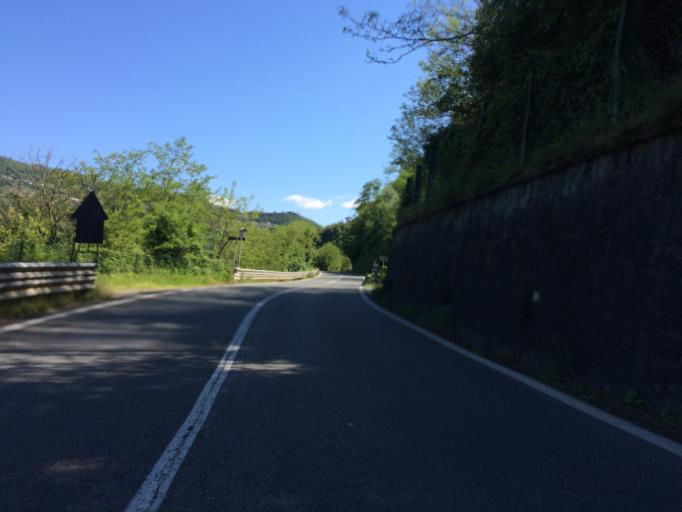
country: IT
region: Tuscany
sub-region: Provincia di Massa-Carrara
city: Podenzana
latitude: 44.1871
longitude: 9.9386
